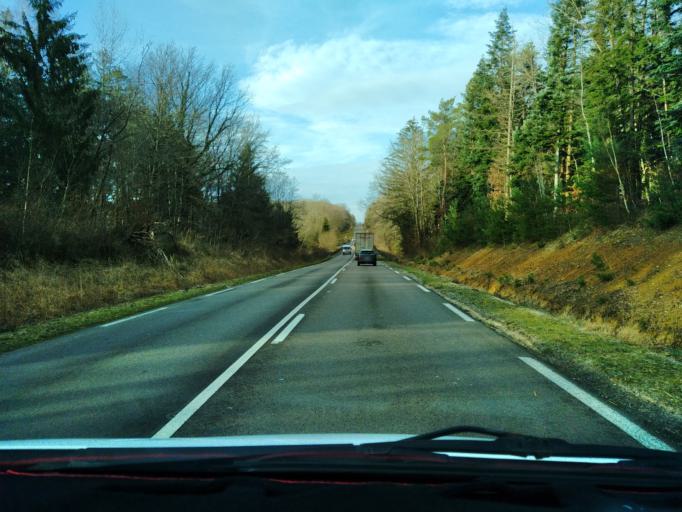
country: FR
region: Franche-Comte
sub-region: Departement de la Haute-Saone
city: Gray
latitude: 47.4036
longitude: 5.6400
